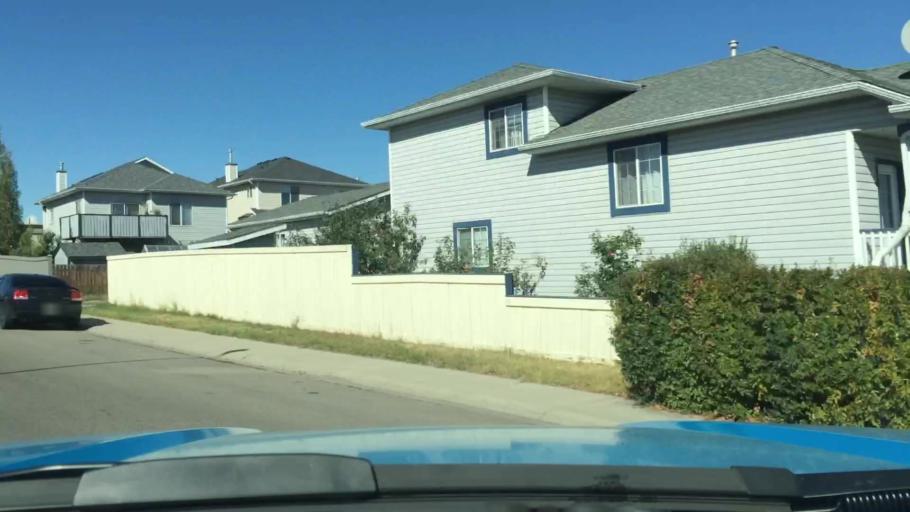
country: CA
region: Alberta
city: Calgary
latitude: 50.9056
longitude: -114.1092
